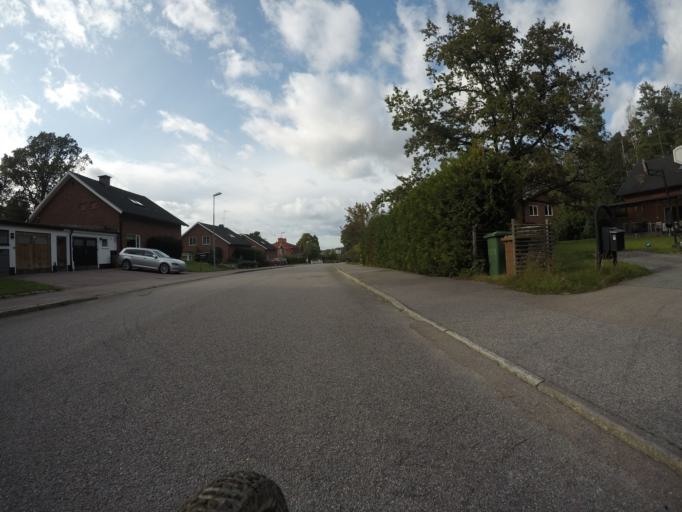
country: SE
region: Vaestmanland
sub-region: Kopings Kommun
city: Koping
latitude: 59.5117
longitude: 16.0137
